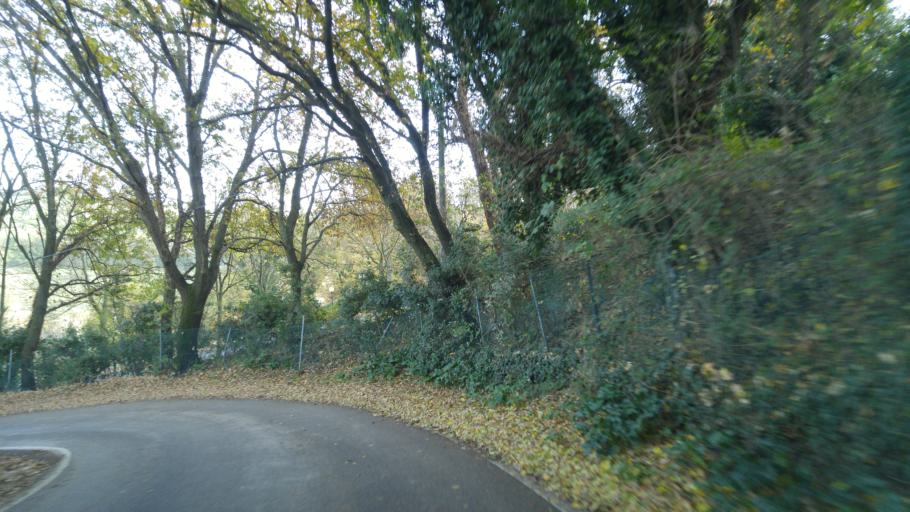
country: IT
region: The Marches
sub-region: Provincia di Pesaro e Urbino
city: Fenile
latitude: 43.8276
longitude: 12.9513
